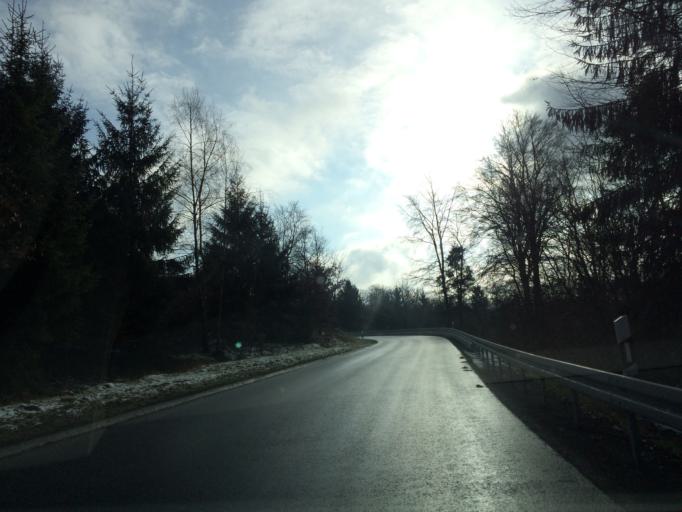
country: DE
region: Hesse
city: Bad Camberg
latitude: 50.3238
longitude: 8.3265
